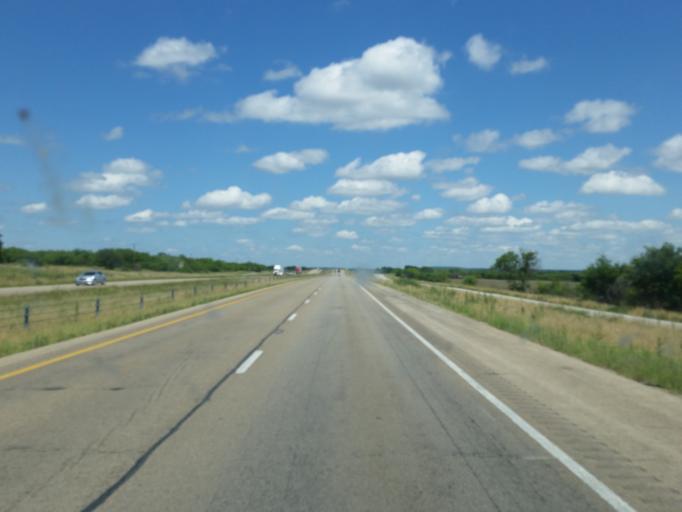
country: US
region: Texas
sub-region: Callahan County
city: Baird
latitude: 32.3870
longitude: -99.3085
